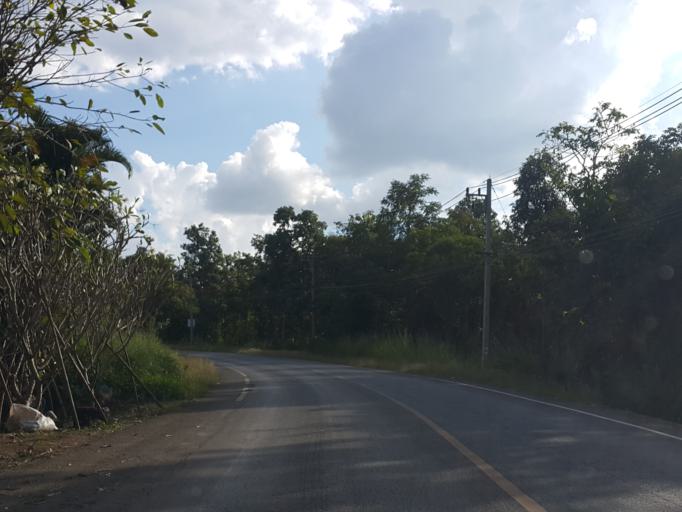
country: TH
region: Chiang Mai
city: Mae On
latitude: 18.8407
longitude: 99.2624
